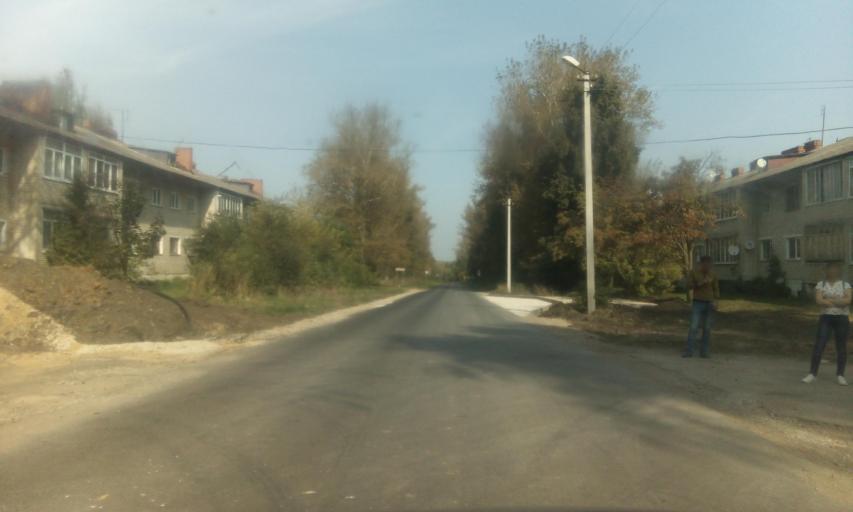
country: RU
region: Tula
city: Partizan
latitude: 53.9531
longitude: 38.0967
